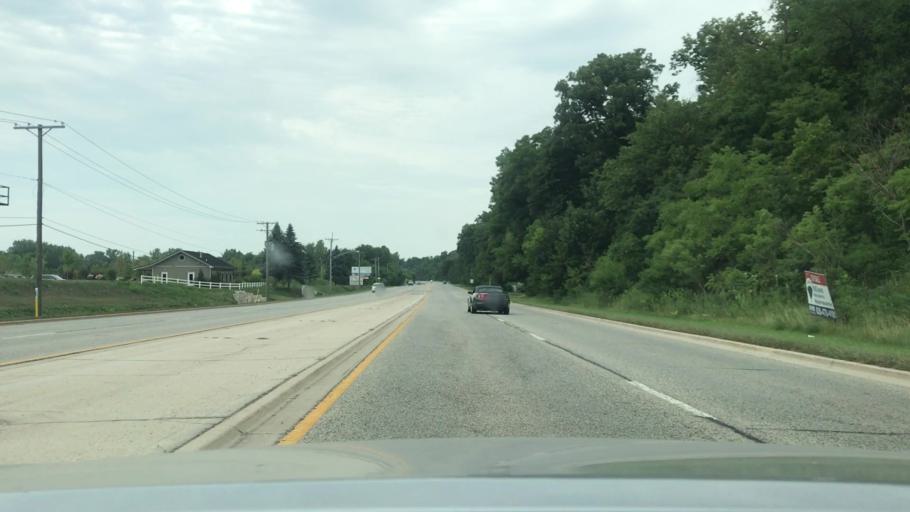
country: US
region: Illinois
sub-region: Will County
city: Bolingbrook
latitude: 41.7239
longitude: -88.0648
